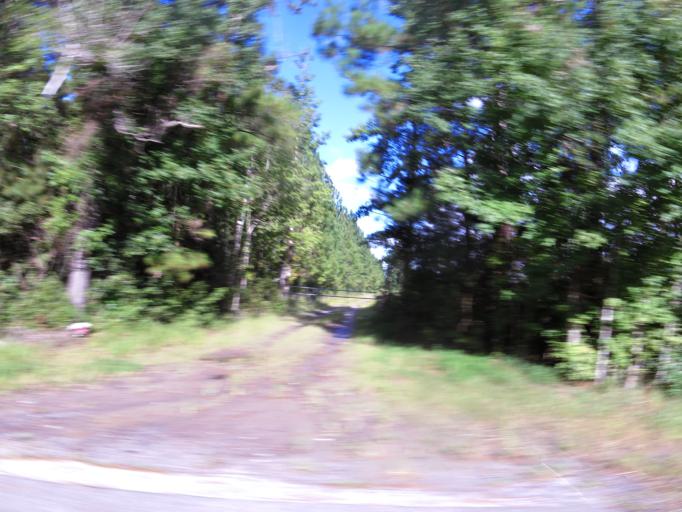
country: US
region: Georgia
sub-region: Camden County
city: Woodbine
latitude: 31.0032
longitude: -81.7319
